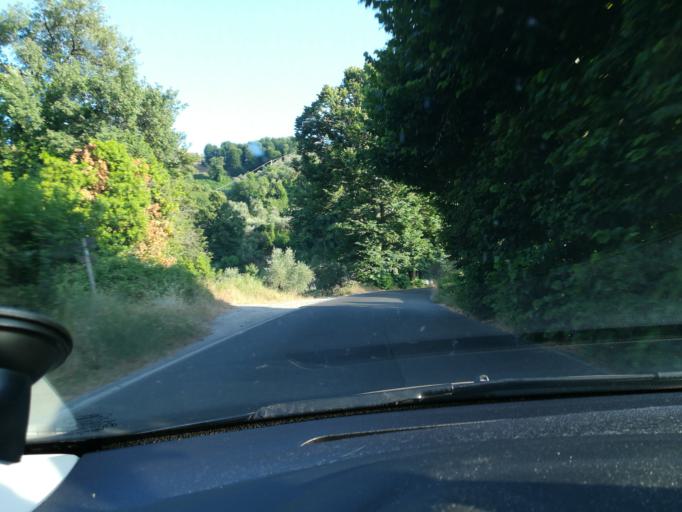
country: IT
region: Tuscany
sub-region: Provincia di Lucca
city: Stiava
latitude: 43.9149
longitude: 10.3403
